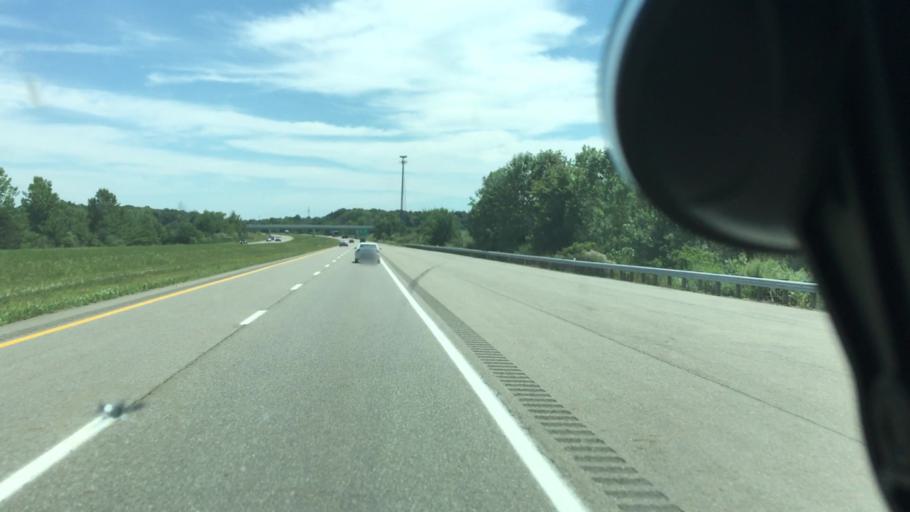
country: US
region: Ohio
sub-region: Columbiana County
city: Columbiana
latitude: 40.9489
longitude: -80.7205
